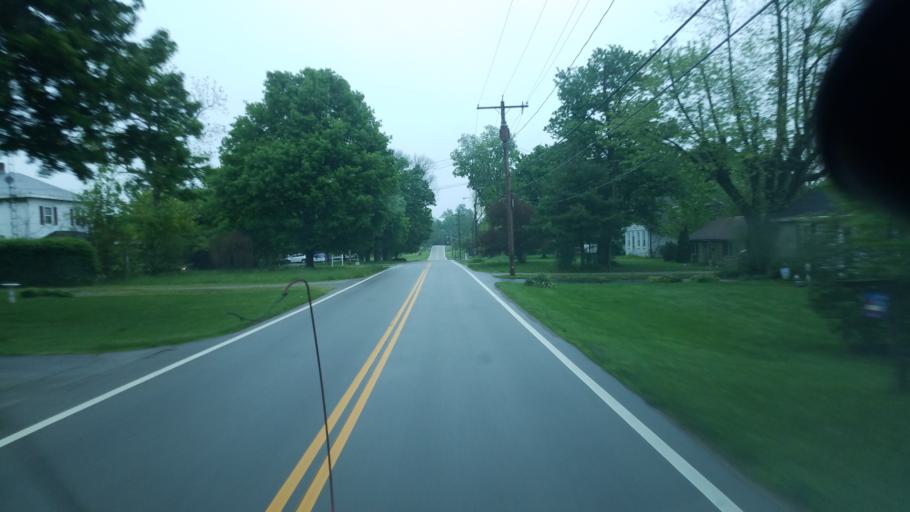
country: US
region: Ohio
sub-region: Highland County
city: Hillsboro
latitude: 39.1989
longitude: -83.6267
